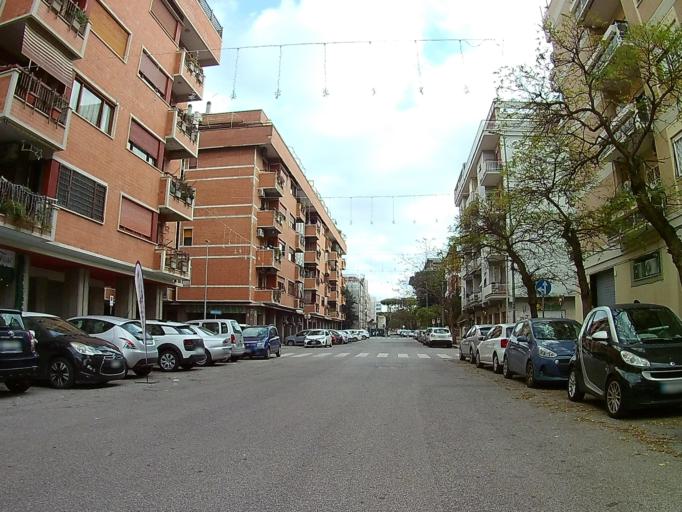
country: IT
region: Latium
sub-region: Citta metropolitana di Roma Capitale
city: Lido di Ostia
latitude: 41.7339
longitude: 12.2892
